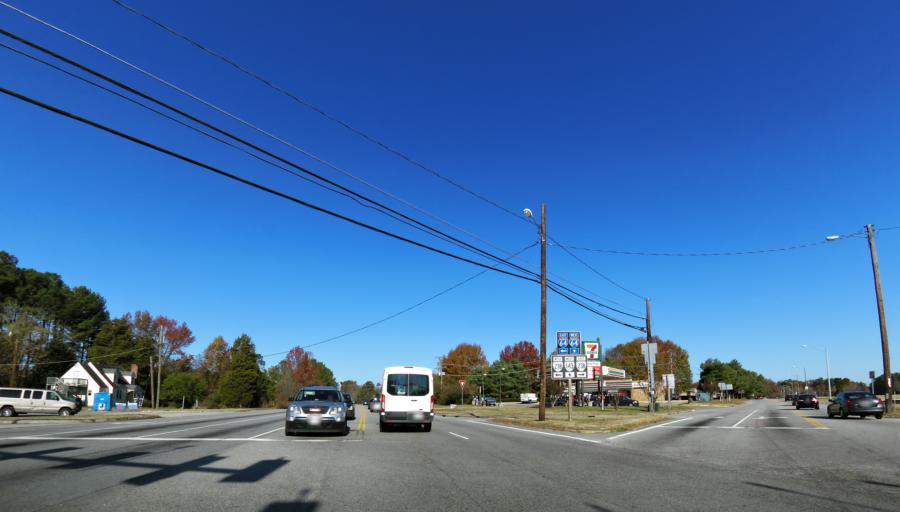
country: US
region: Virginia
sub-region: York County
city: Yorktown
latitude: 37.2070
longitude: -76.5738
